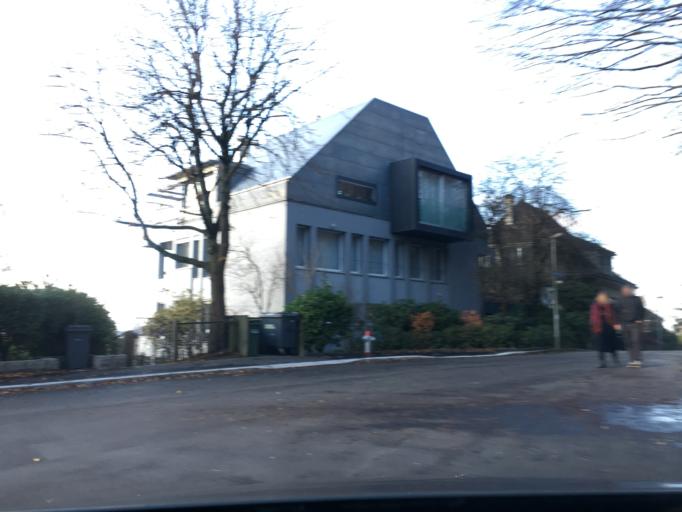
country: CH
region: Zurich
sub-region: Bezirk Zuerich
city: Zuerich (Kreis 6) / Oberstrass
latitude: 47.3886
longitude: 8.5528
